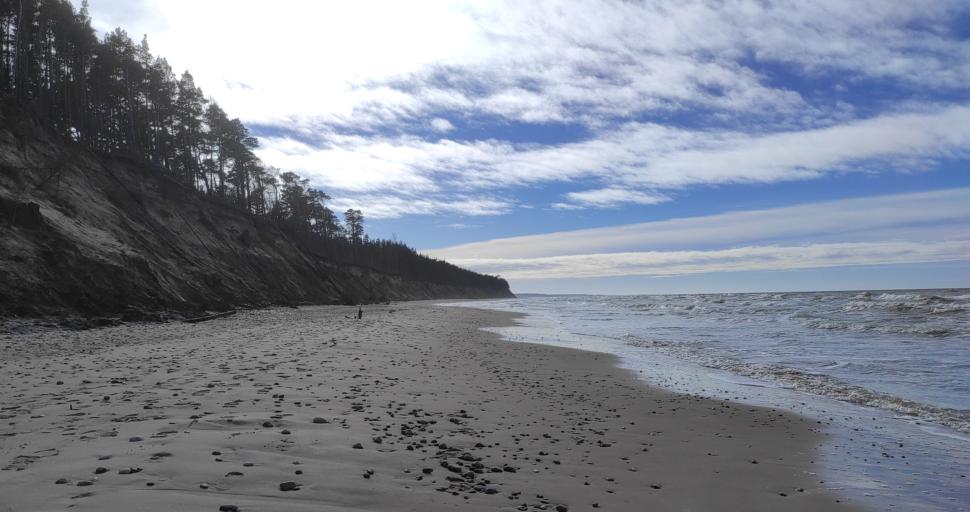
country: LV
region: Alsunga
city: Alsunga
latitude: 57.0283
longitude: 21.3963
